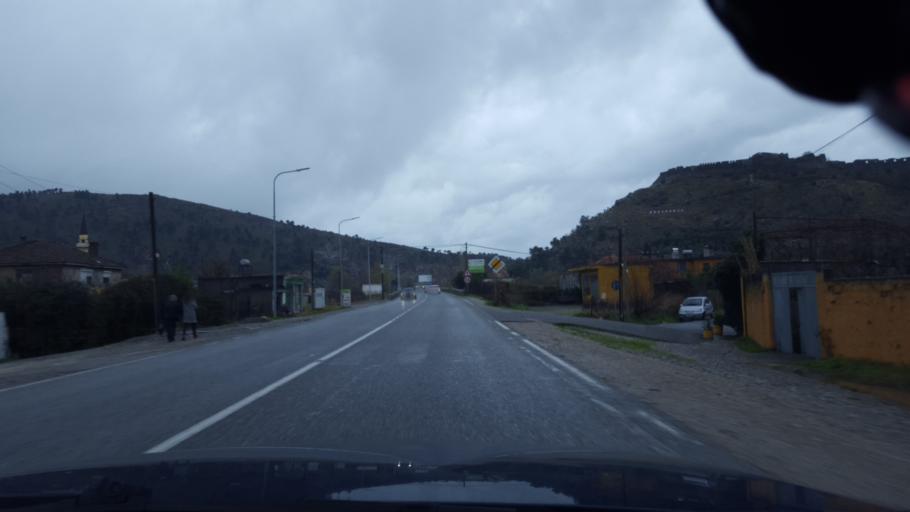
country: AL
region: Shkoder
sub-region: Rrethi i Shkodres
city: Berdica e Madhe
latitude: 42.0401
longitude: 19.4951
